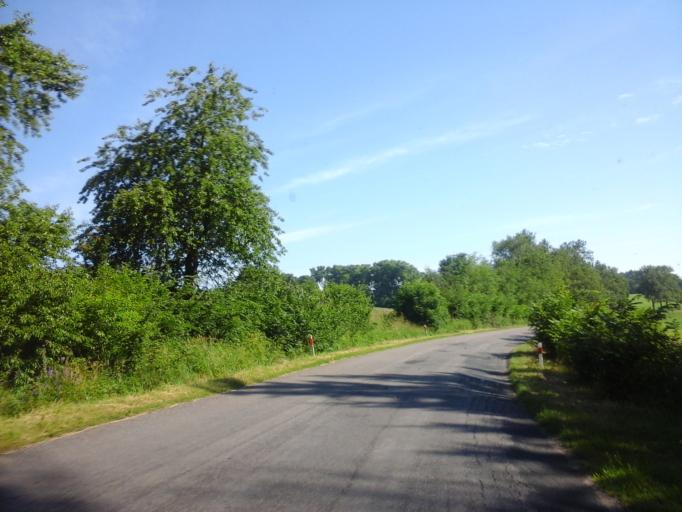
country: PL
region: West Pomeranian Voivodeship
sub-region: Powiat swidwinski
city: Polczyn-Zdroj
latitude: 53.6832
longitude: 16.0207
